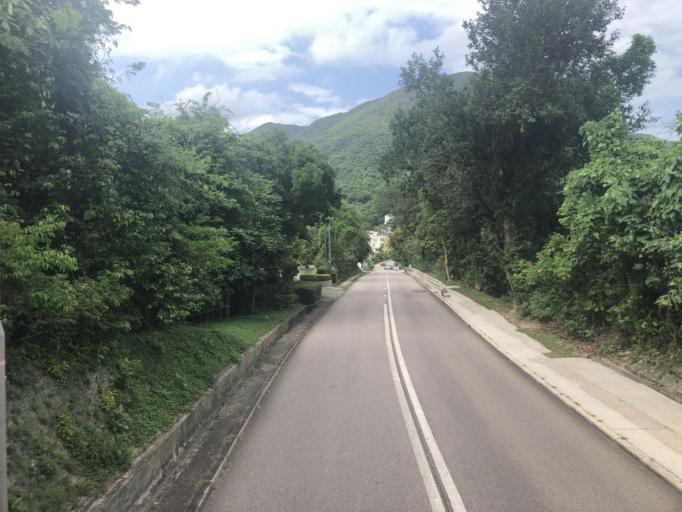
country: HK
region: Sai Kung
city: Sai Kung
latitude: 22.3893
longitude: 114.3075
